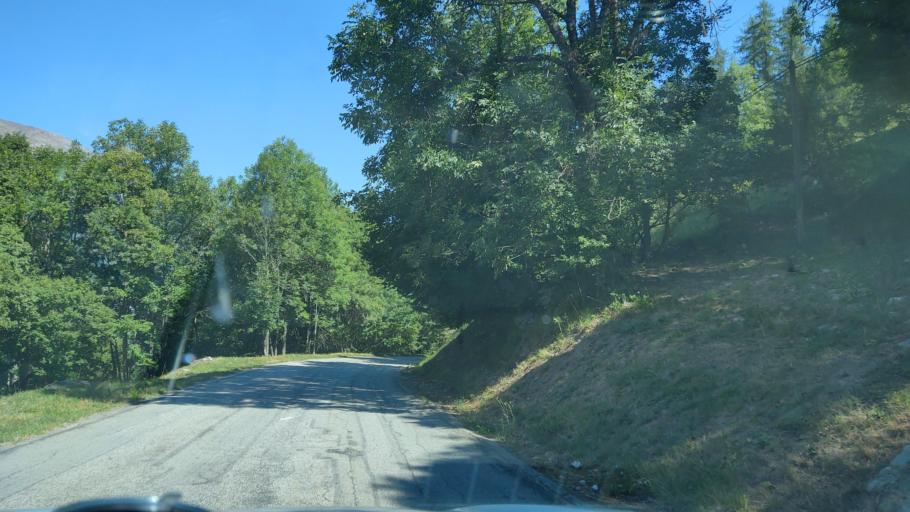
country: FR
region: Rhone-Alpes
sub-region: Departement de la Savoie
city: Saint-Martin-de-Belleville
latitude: 45.4133
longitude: 6.4943
